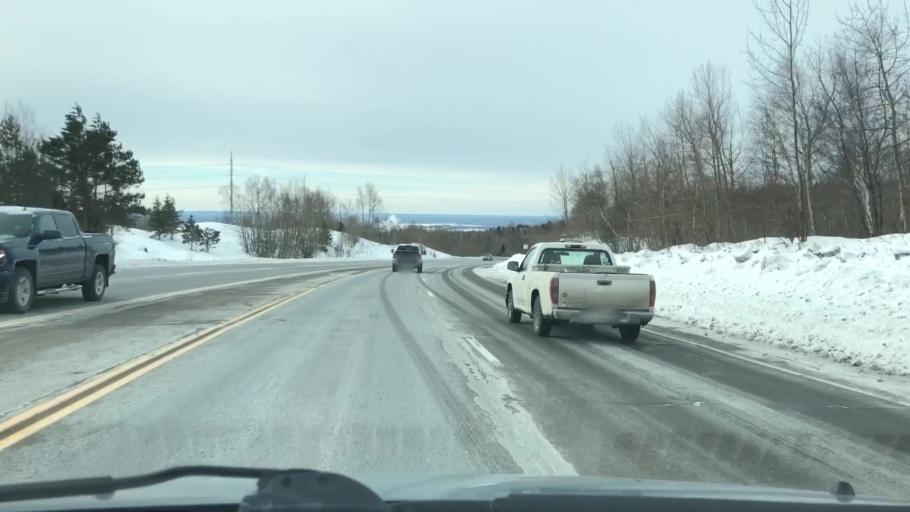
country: US
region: Minnesota
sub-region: Saint Louis County
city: Duluth
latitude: 46.7806
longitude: -92.1391
